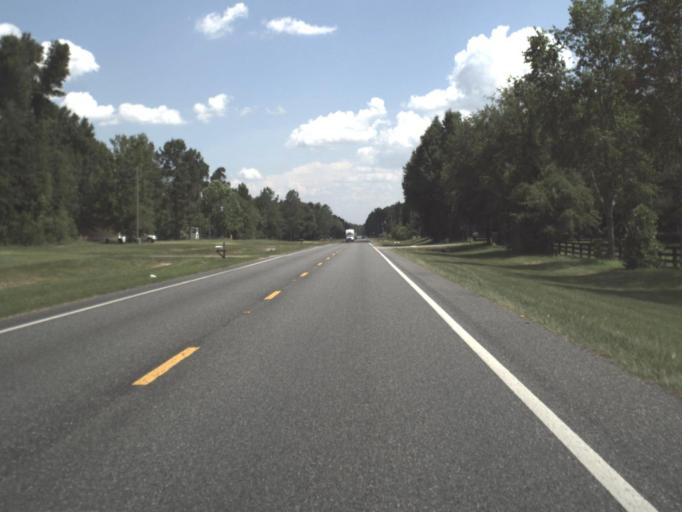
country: US
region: Florida
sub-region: Alachua County
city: High Springs
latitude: 29.8677
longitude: -82.6088
